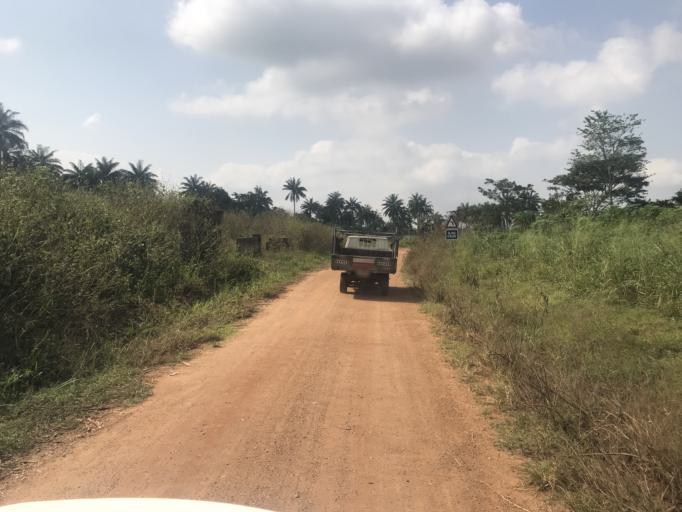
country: NG
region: Osun
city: Ikirun
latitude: 7.8568
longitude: 4.6307
